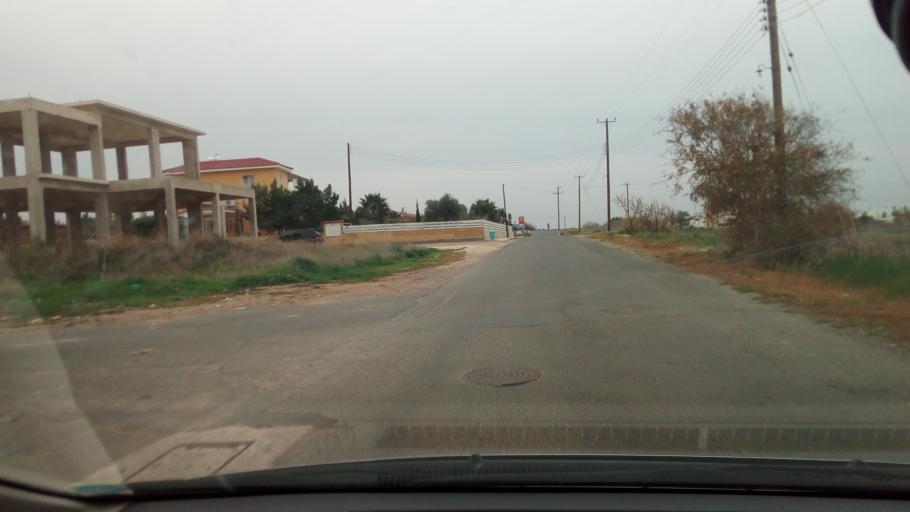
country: CY
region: Pafos
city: Empa
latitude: 34.8045
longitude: 32.4191
